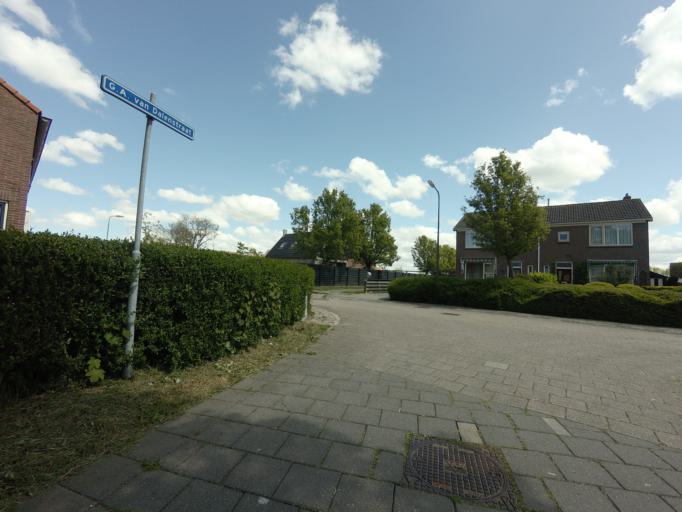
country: NL
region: Friesland
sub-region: Gemeente Franekeradeel
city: Franeker
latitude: 53.1481
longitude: 5.4877
